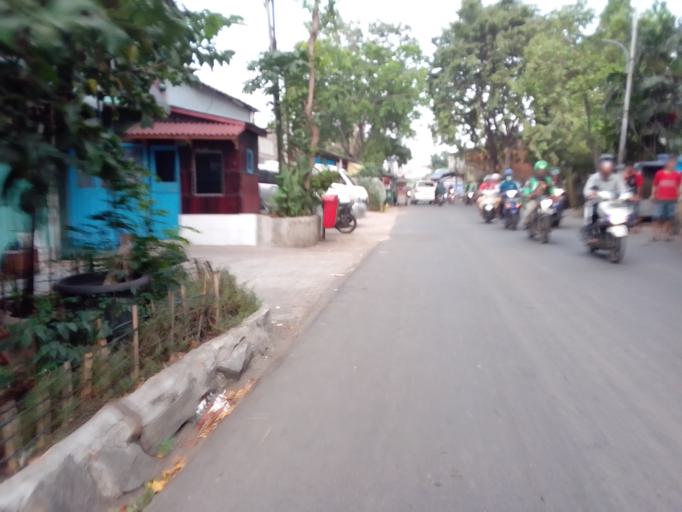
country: ID
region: Jakarta Raya
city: Jakarta
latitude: -6.1613
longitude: 106.8029
